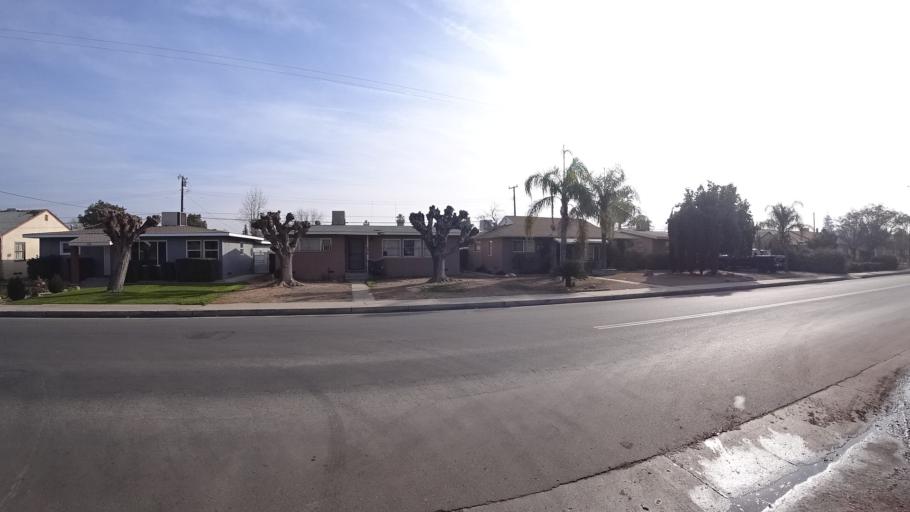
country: US
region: California
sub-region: Kern County
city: Bakersfield
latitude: 35.3592
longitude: -119.0436
